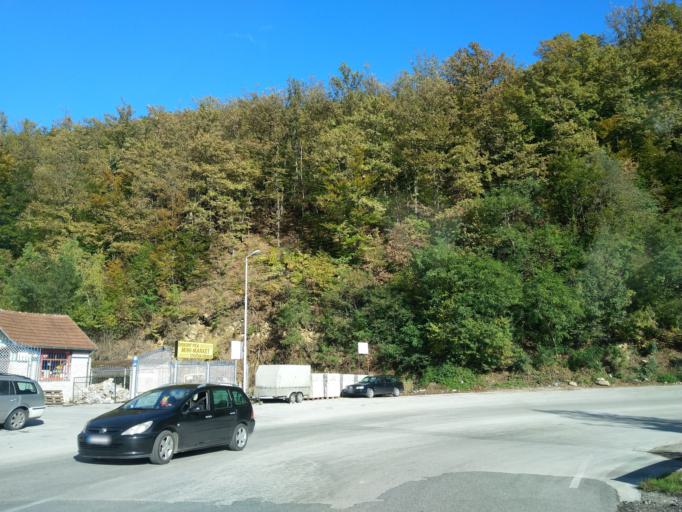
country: RS
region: Central Serbia
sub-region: Zlatiborski Okrug
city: Uzice
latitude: 43.8666
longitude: 19.8147
